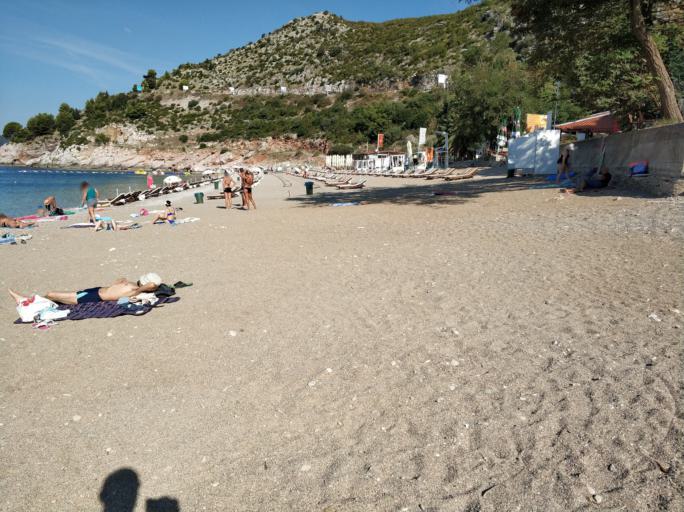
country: ME
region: Budva
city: Budva
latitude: 42.2745
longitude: 18.8881
